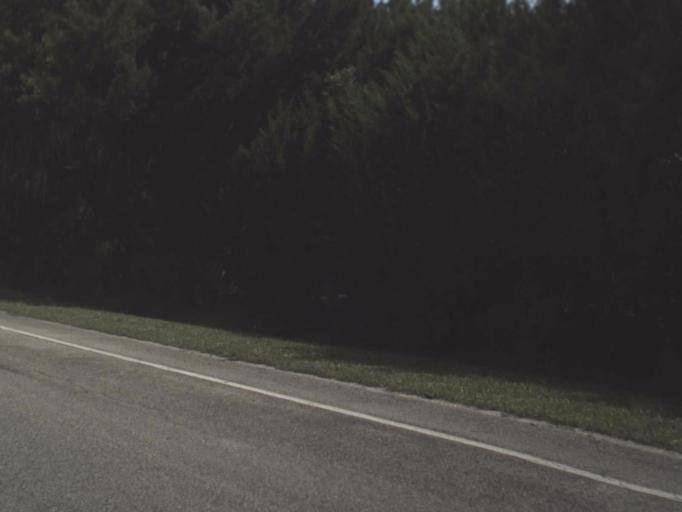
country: US
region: Florida
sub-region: Alachua County
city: Hawthorne
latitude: 29.5054
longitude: -82.0994
